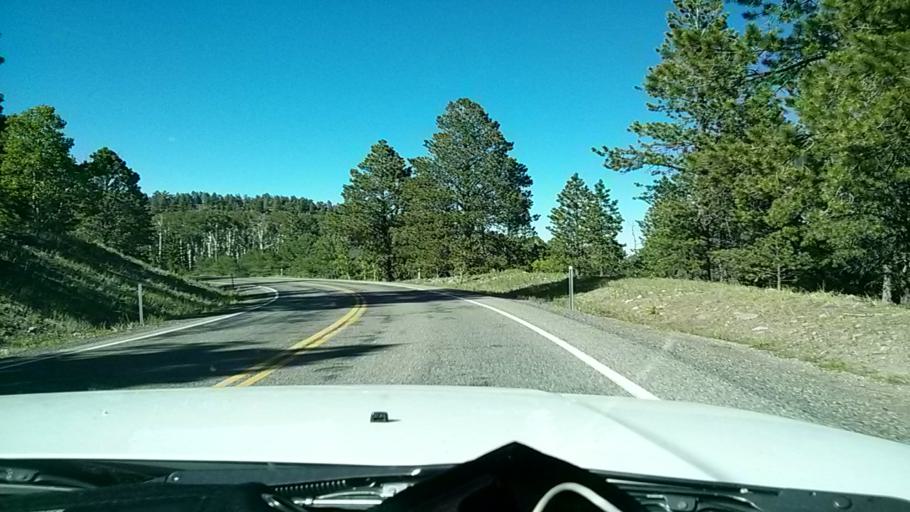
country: US
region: Utah
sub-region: Wayne County
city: Loa
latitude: 38.0831
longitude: -111.3375
